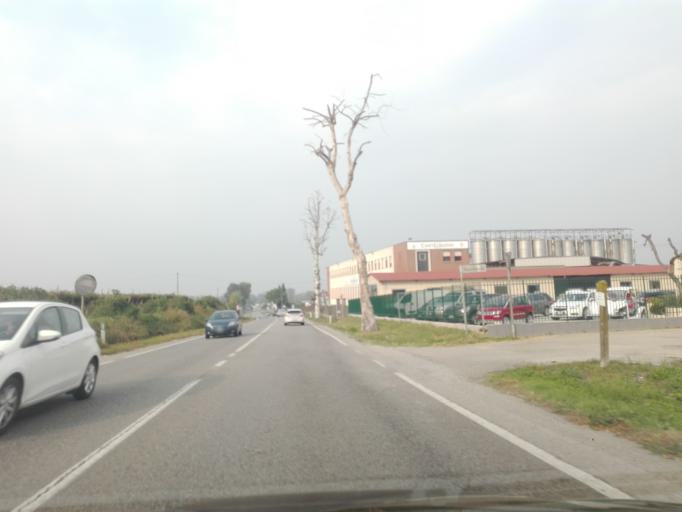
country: IT
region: Veneto
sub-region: Provincia di Verona
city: San Giorgio in Salici
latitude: 45.4396
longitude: 10.7847
